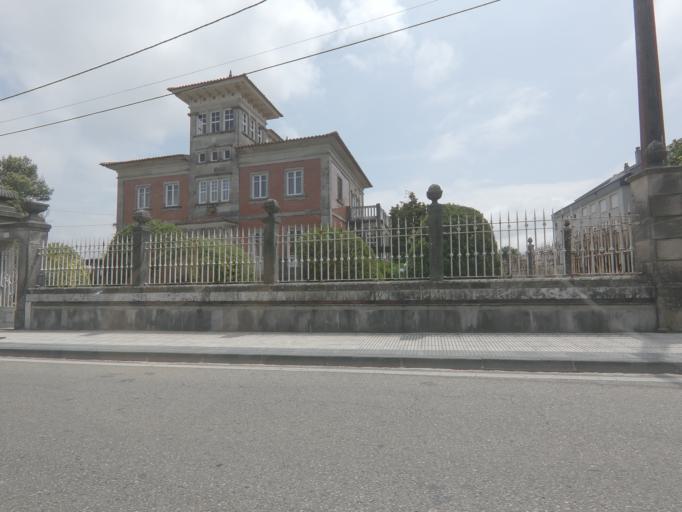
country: ES
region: Galicia
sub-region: Provincia de Pontevedra
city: A Guarda
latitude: 41.9049
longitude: -8.8649
